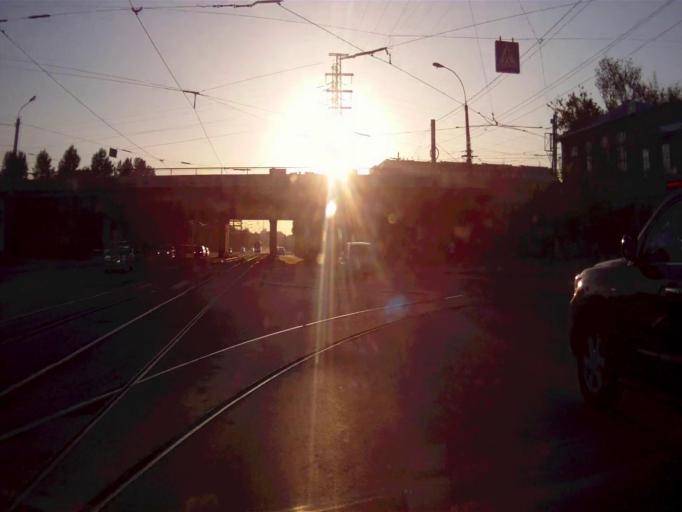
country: RU
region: Chelyabinsk
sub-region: Gorod Chelyabinsk
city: Chelyabinsk
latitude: 55.1682
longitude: 61.4296
